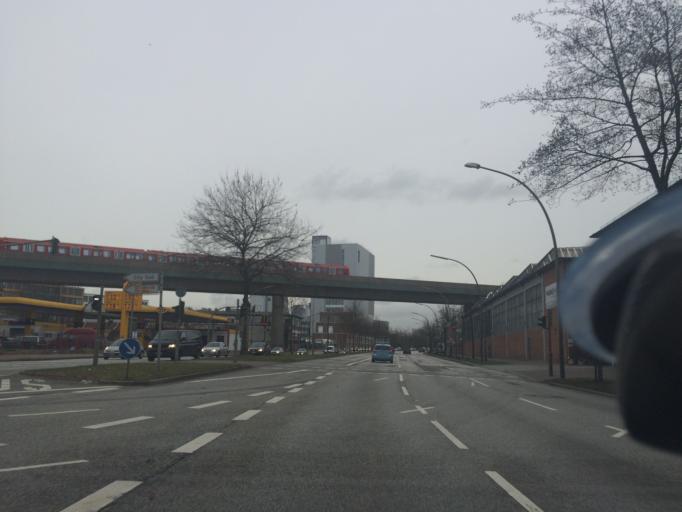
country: DE
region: Hamburg
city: Hammerbrook
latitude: 53.5427
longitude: 10.0247
